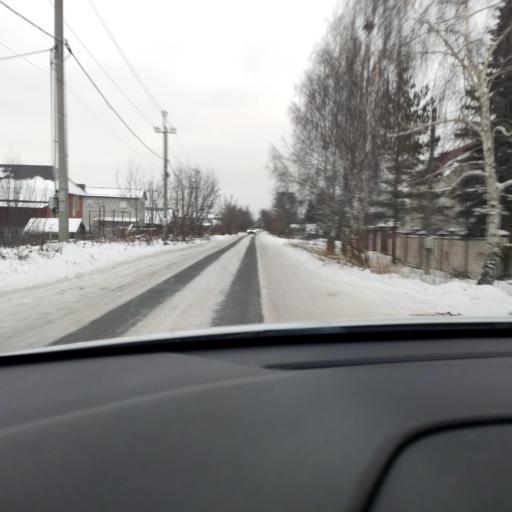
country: RU
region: Tatarstan
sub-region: Gorod Kazan'
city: Kazan
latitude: 55.8730
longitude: 49.1498
